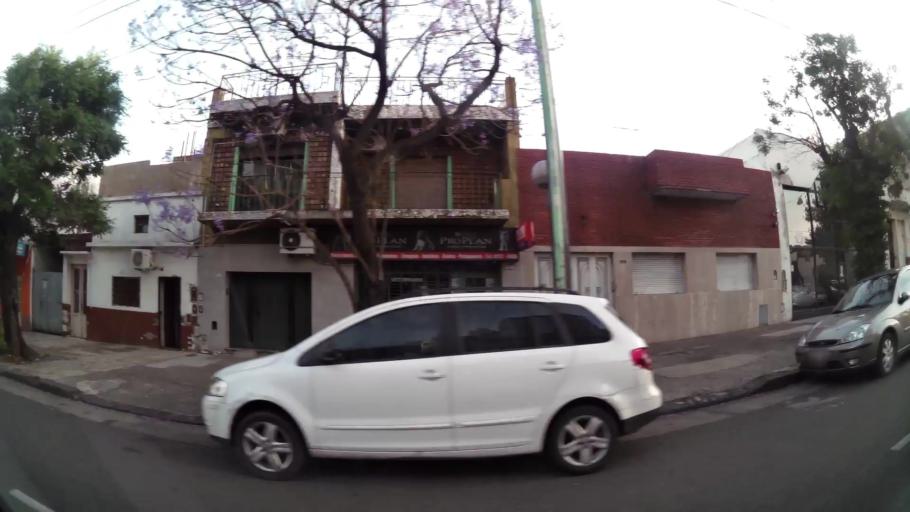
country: AR
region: Buenos Aires F.D.
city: Buenos Aires
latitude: -34.6404
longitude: -58.4245
